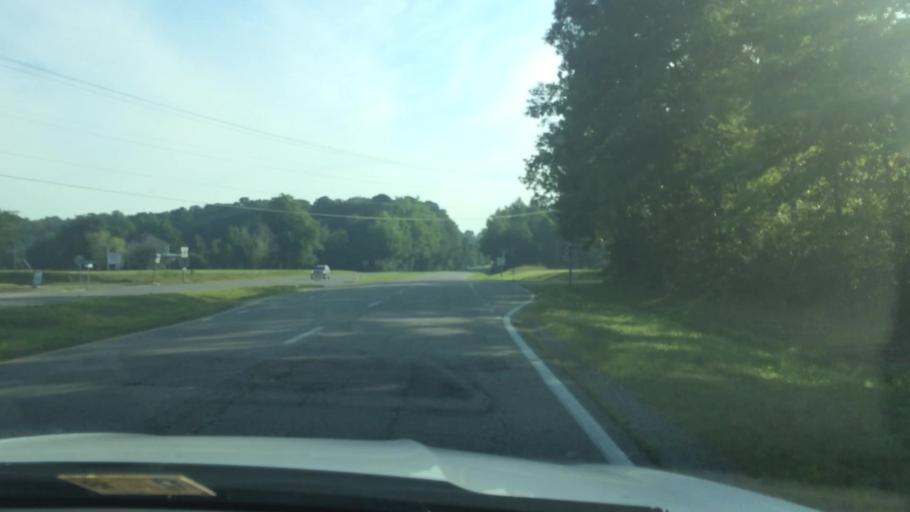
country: US
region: Virginia
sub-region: Gloucester County
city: Gloucester Courthouse
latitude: 37.4185
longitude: -76.5148
